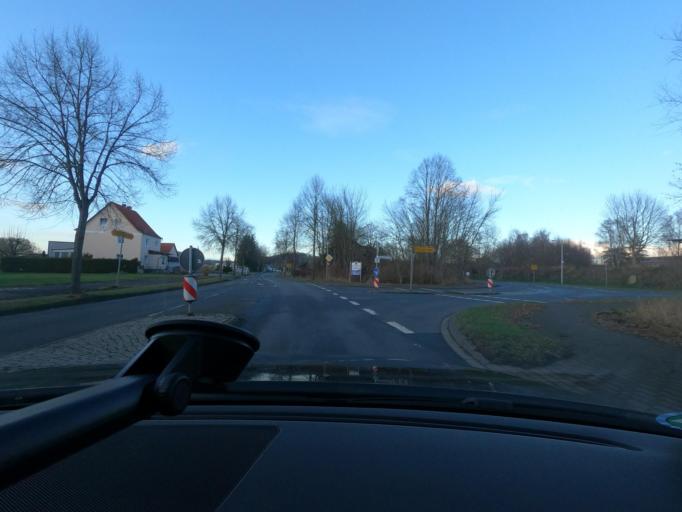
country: DE
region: Lower Saxony
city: Rhumspringe
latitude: 51.5761
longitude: 10.2969
